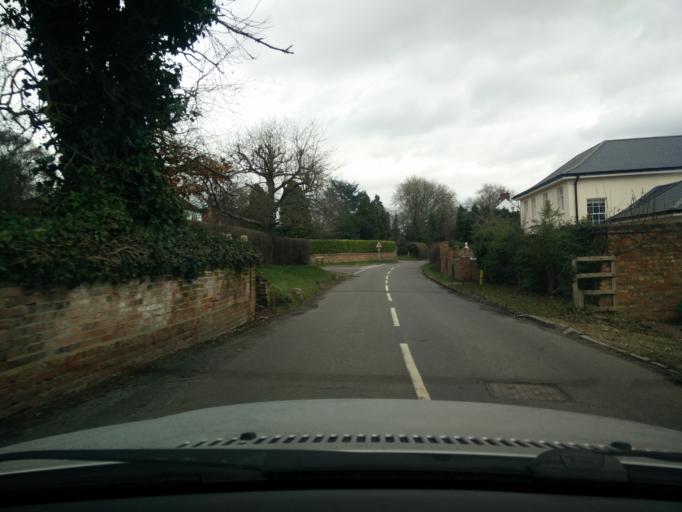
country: GB
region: England
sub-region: Buckinghamshire
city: Amersham
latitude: 51.6528
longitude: -0.6247
